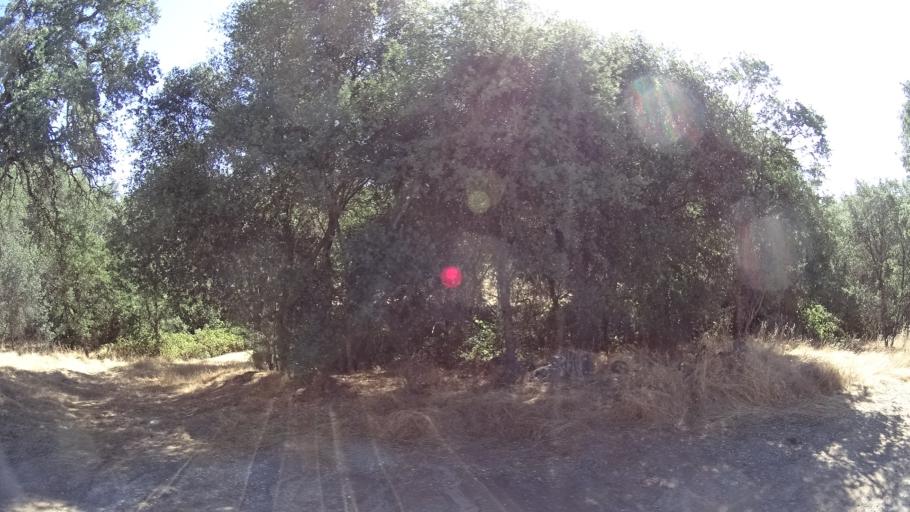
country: US
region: California
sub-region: Calaveras County
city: Angels Camp
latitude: 38.0781
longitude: -120.5431
